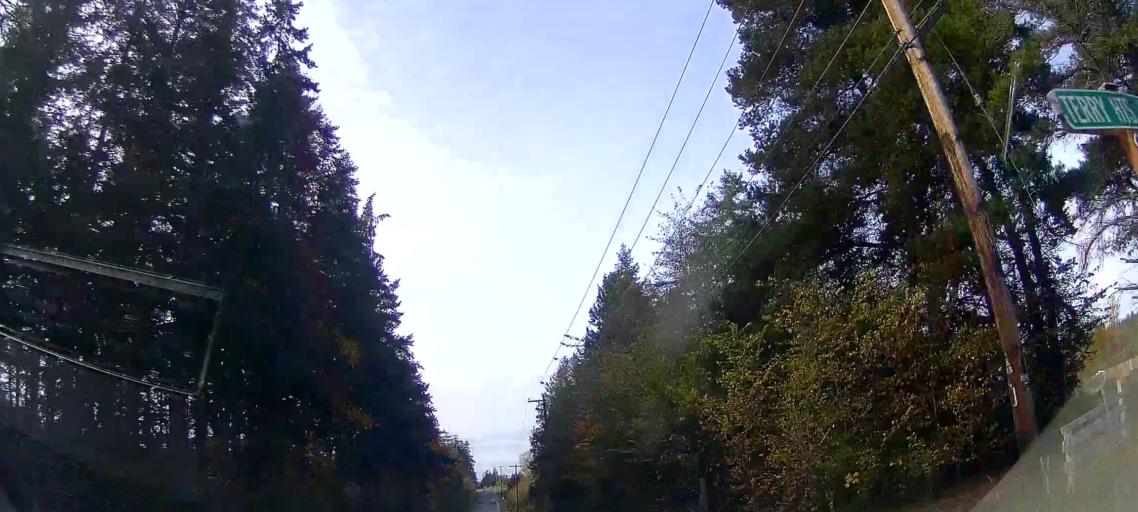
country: US
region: Washington
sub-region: Snohomish County
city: Stanwood
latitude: 48.2502
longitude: -122.4642
